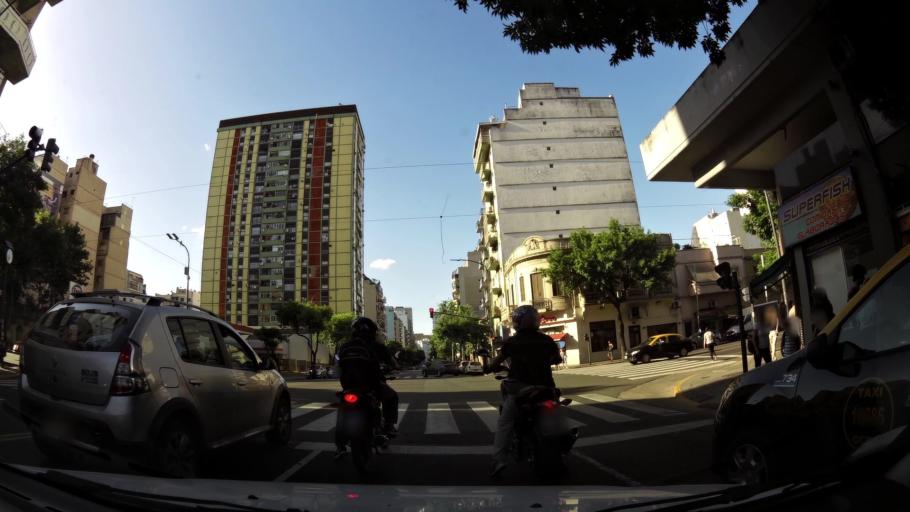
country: AR
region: Buenos Aires F.D.
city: Buenos Aires
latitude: -34.6223
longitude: -58.4277
